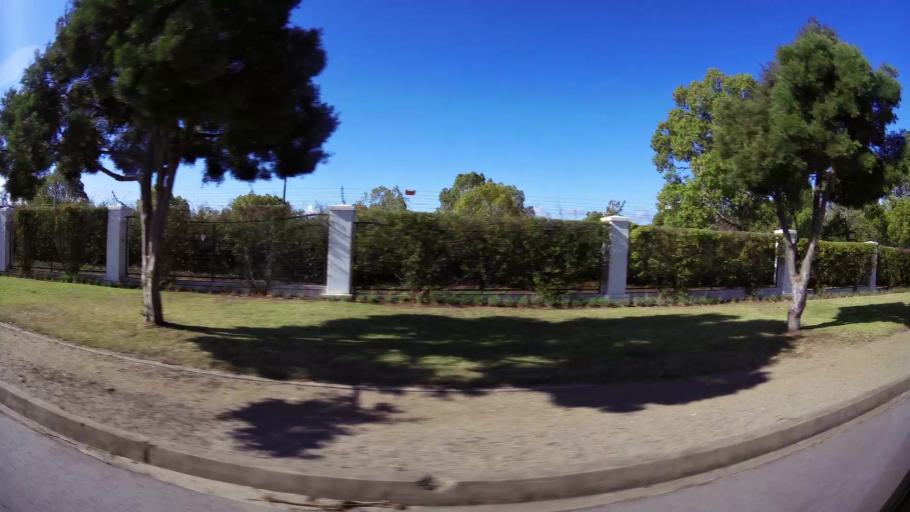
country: ZA
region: Western Cape
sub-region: Eden District Municipality
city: George
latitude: -33.9498
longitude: 22.4078
